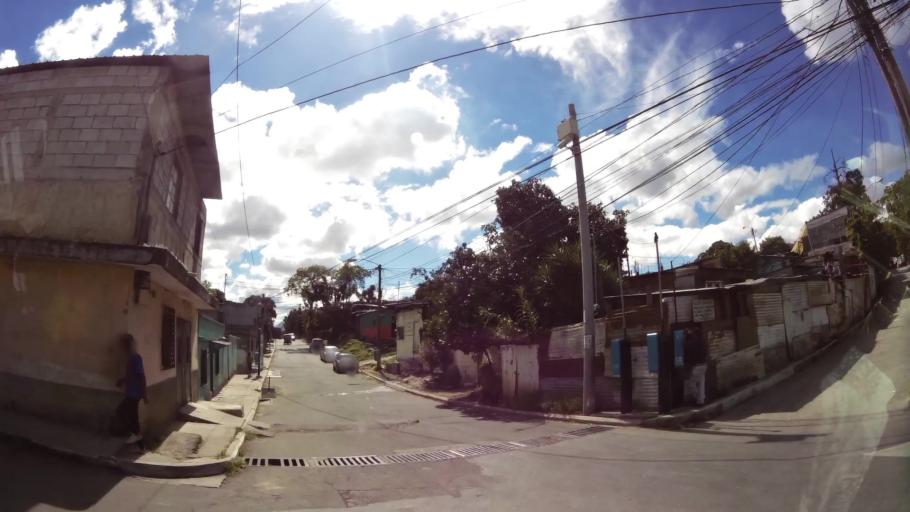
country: GT
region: Guatemala
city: Santa Catarina Pinula
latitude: 14.5545
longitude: -90.5413
